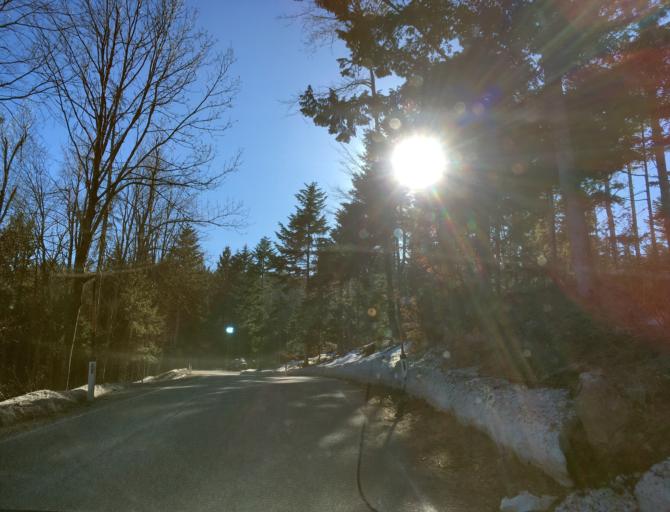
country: AT
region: Lower Austria
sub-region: Politischer Bezirk Wiener Neustadt
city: Waldegg
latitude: 47.8393
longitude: 16.0538
